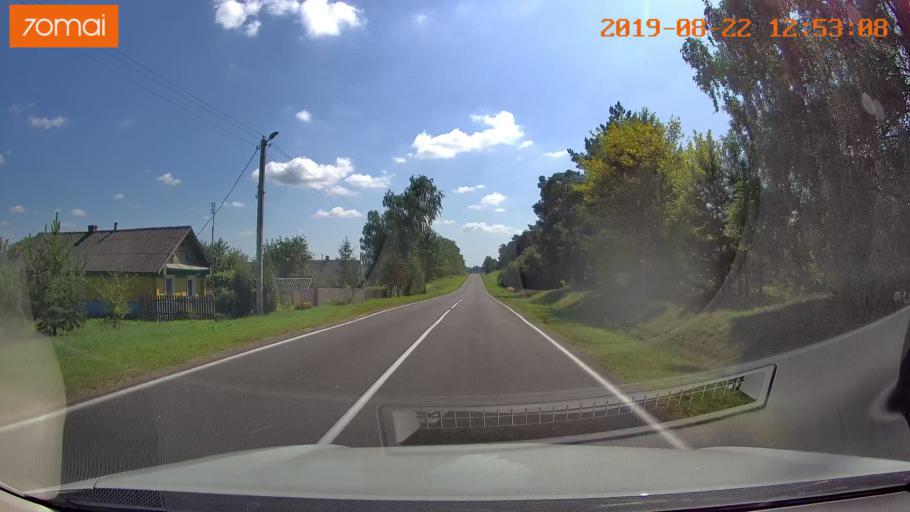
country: BY
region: Minsk
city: Prawdzinski
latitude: 53.4497
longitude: 27.6826
